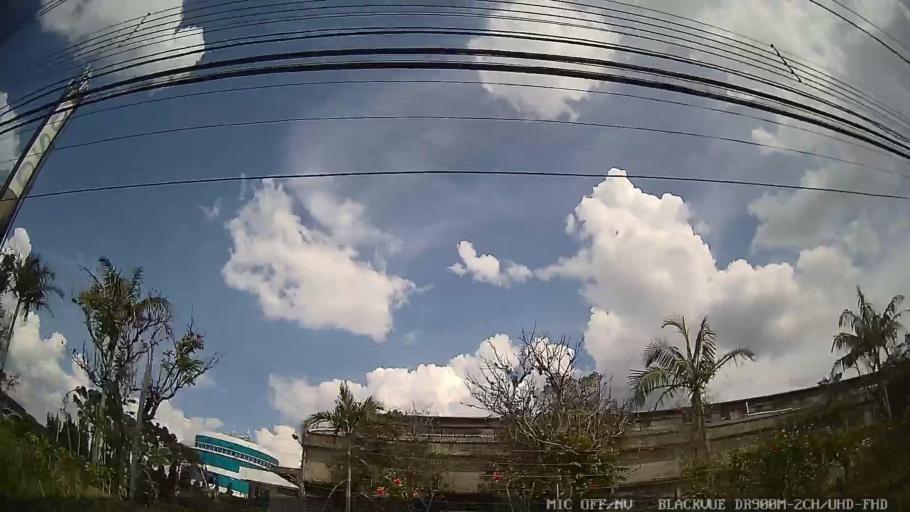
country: BR
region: Sao Paulo
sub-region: Braganca Paulista
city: Braganca Paulista
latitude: -22.9745
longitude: -46.5521
